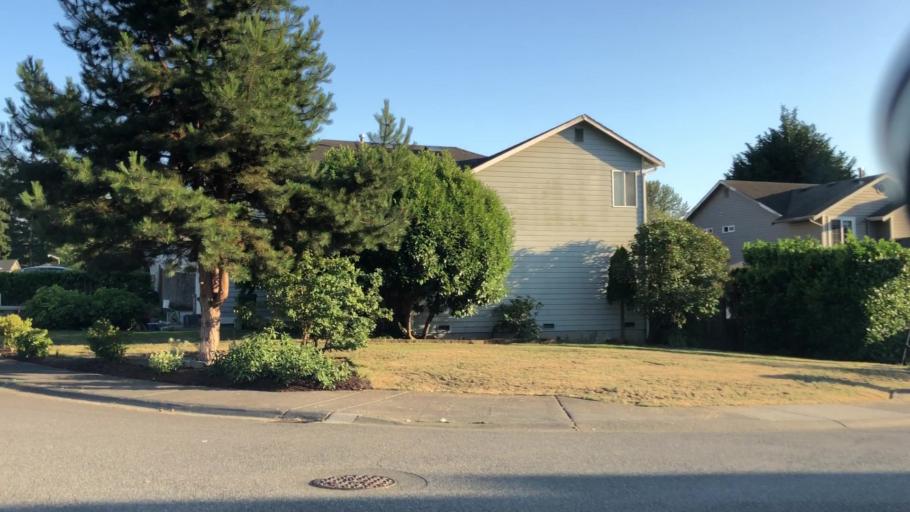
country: US
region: Washington
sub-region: Snohomish County
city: Martha Lake
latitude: 47.8629
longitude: -122.2634
